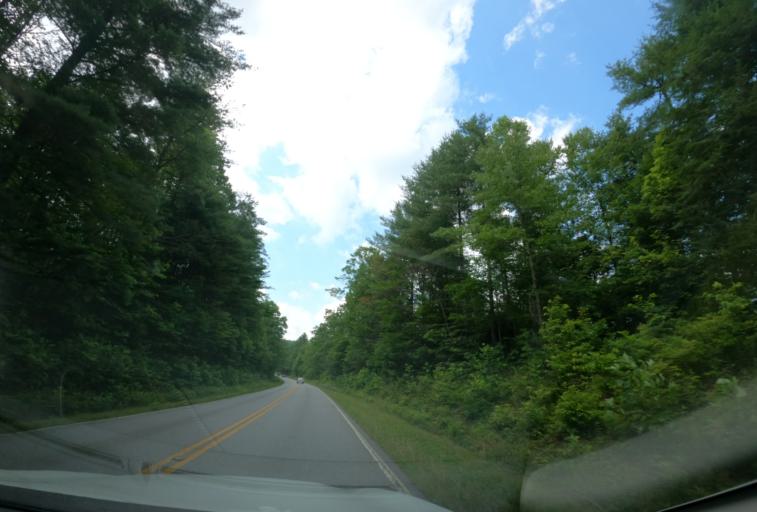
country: US
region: South Carolina
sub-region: Oconee County
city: Walhalla
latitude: 35.0465
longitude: -83.0108
